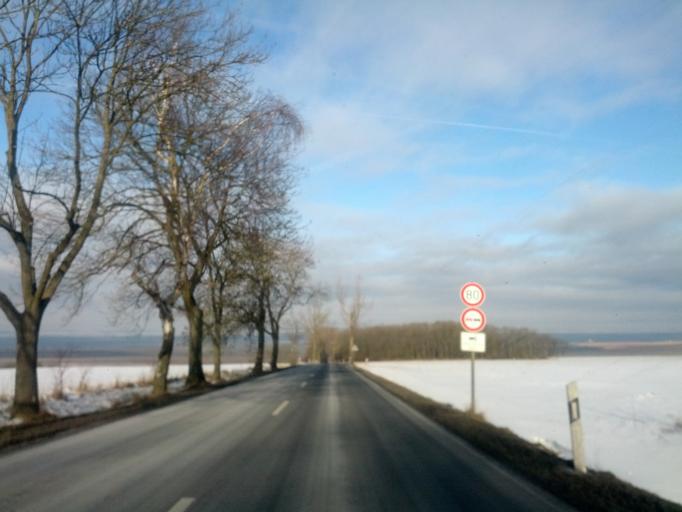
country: DE
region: Thuringia
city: Wangenheim
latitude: 51.0634
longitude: 10.5865
